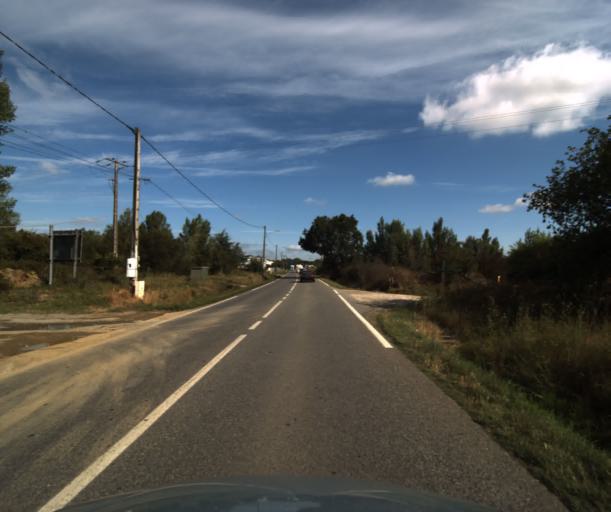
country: FR
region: Midi-Pyrenees
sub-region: Departement de la Haute-Garonne
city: Seysses
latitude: 43.4863
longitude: 1.3183
